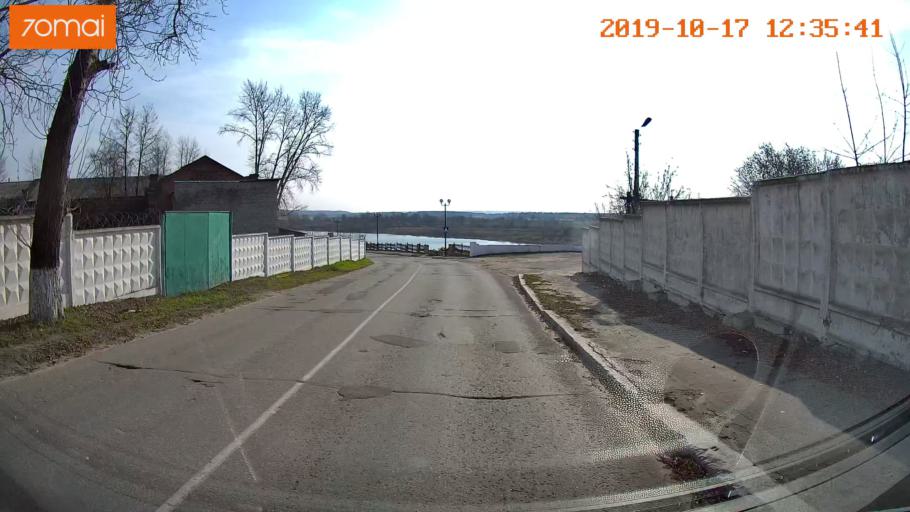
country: RU
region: Rjazan
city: Kasimov
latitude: 54.9424
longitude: 41.3707
